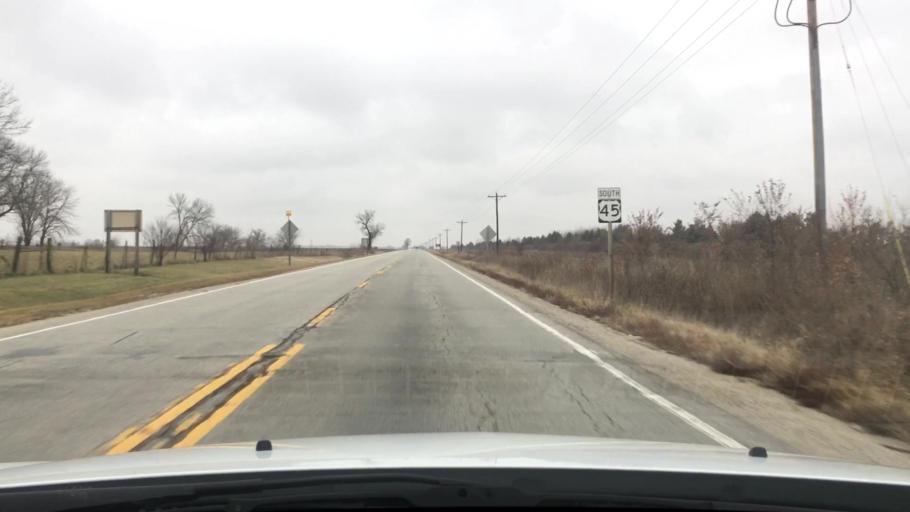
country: US
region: Illinois
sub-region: Iroquois County
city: Clifton
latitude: 40.8872
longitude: -87.8669
